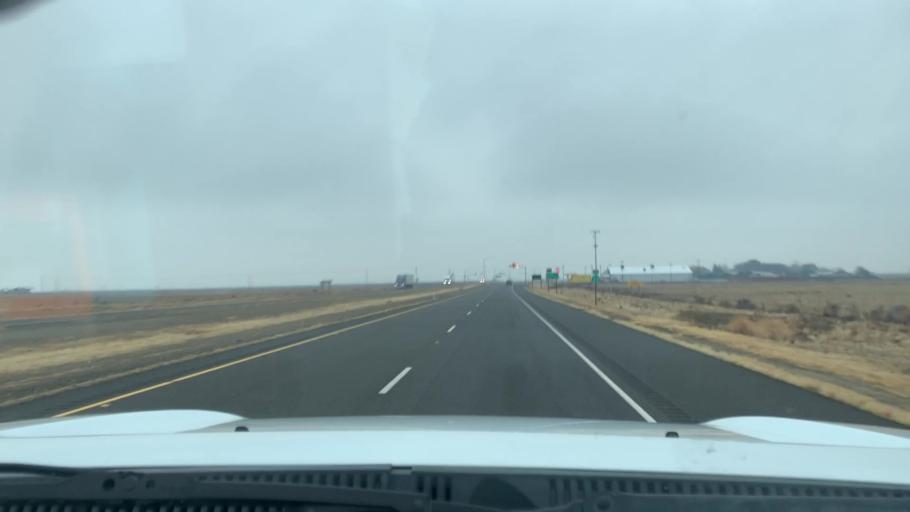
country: US
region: California
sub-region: Kern County
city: Lost Hills
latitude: 35.6148
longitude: -119.8740
